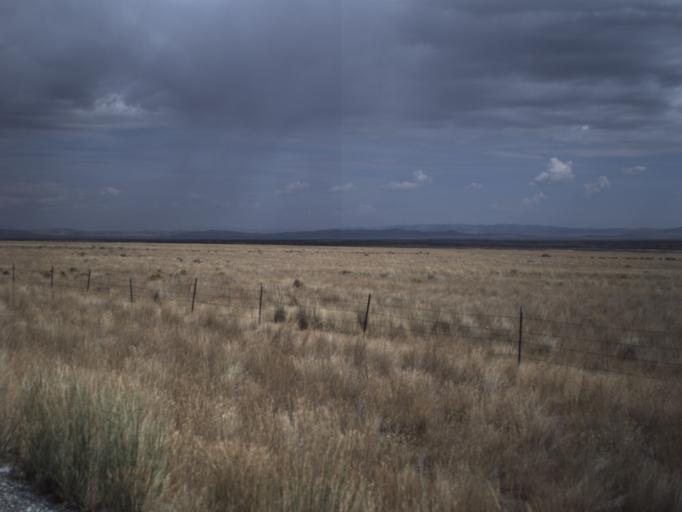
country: US
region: Idaho
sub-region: Oneida County
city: Malad City
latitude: 41.8781
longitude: -113.1190
